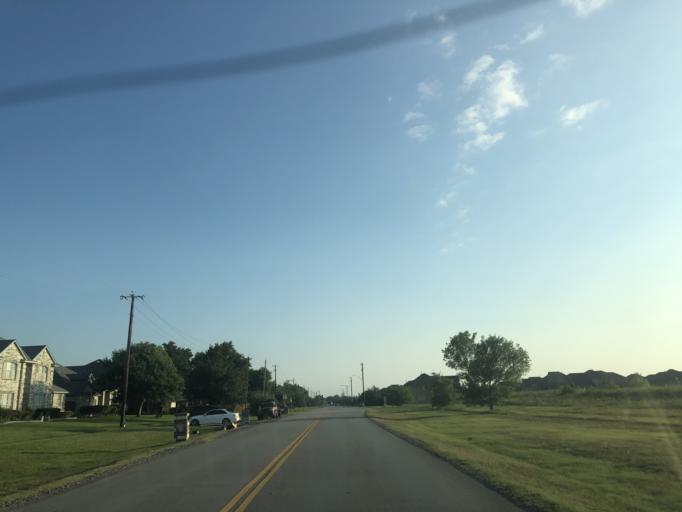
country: US
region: Texas
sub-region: Dallas County
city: Sunnyvale
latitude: 32.8394
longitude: -96.5606
